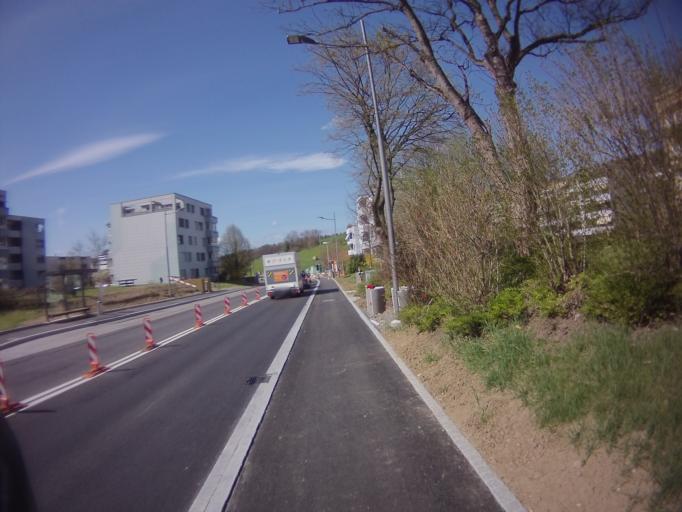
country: CH
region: Aargau
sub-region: Bezirk Baden
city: Niederrohrdorf
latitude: 47.4238
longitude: 8.3117
